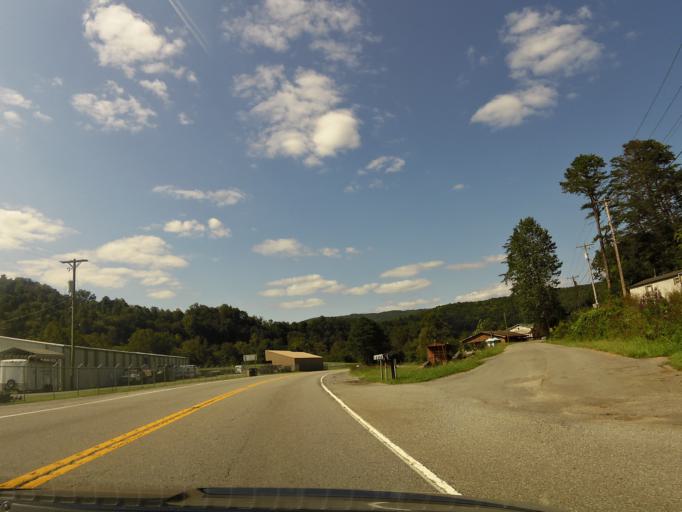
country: US
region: Kentucky
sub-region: Bell County
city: Pineville
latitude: 36.7228
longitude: -83.6418
